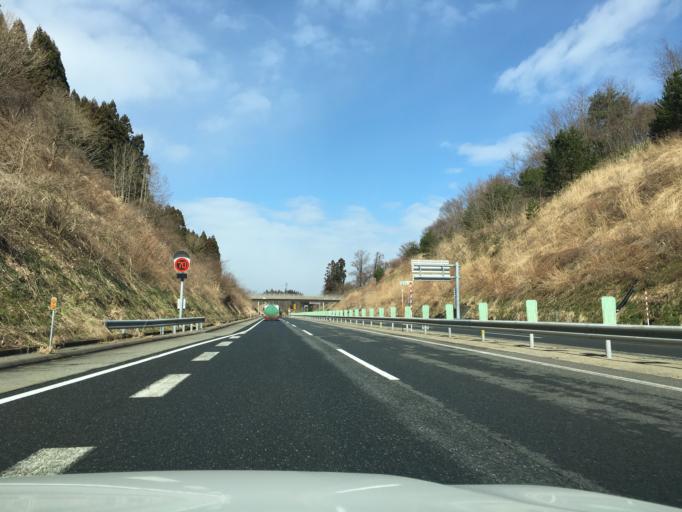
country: JP
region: Akita
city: Akita Shi
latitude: 39.7839
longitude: 140.1102
